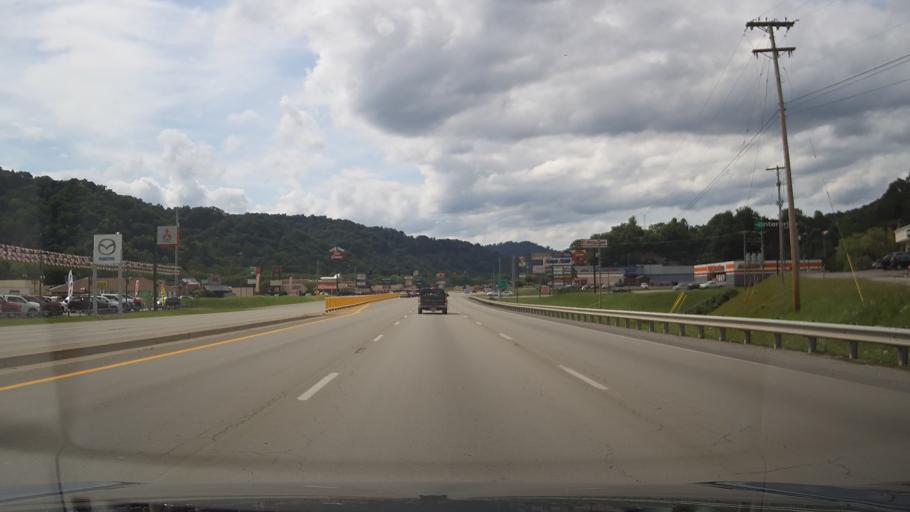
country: US
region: Kentucky
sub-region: Pike County
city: Coal Run Village
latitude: 37.5210
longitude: -82.5688
